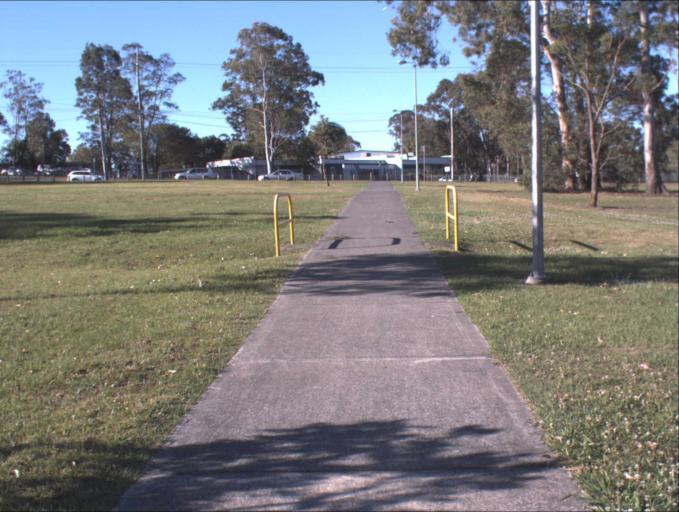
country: AU
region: Queensland
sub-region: Logan
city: Logan City
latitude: -27.6408
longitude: 153.1292
